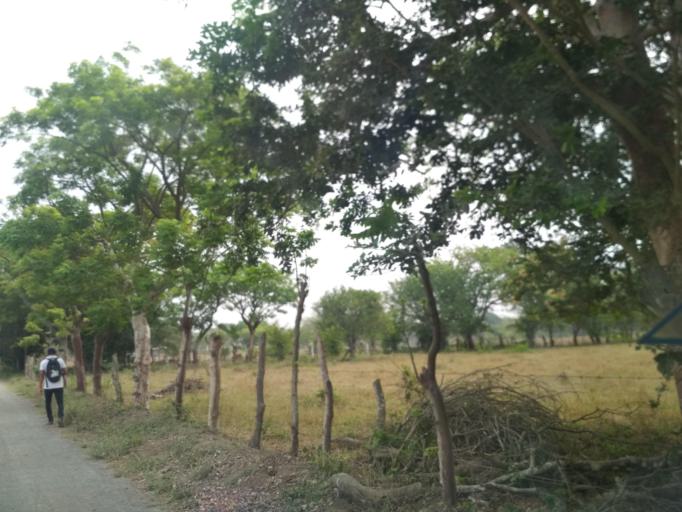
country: MX
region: Veracruz
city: Paso del Toro
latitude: 19.0179
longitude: -96.1502
